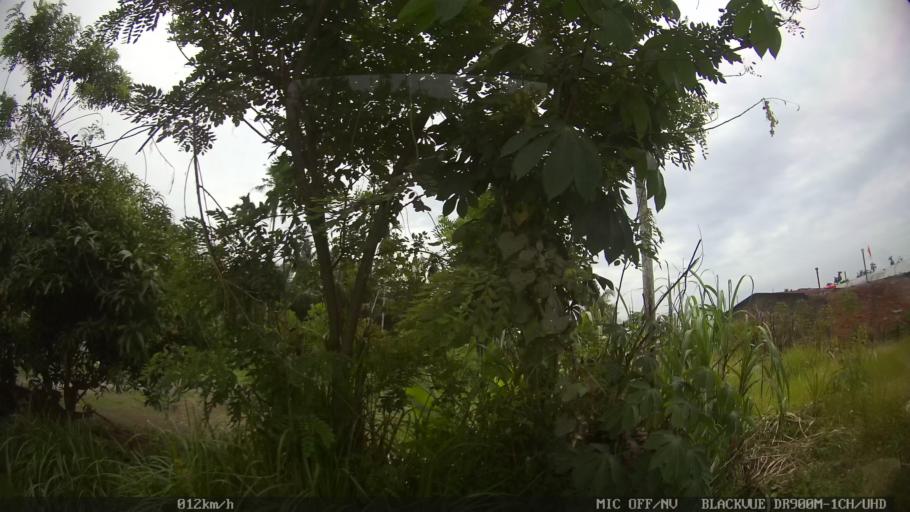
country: ID
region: North Sumatra
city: Binjai
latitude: 3.6197
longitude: 98.5544
